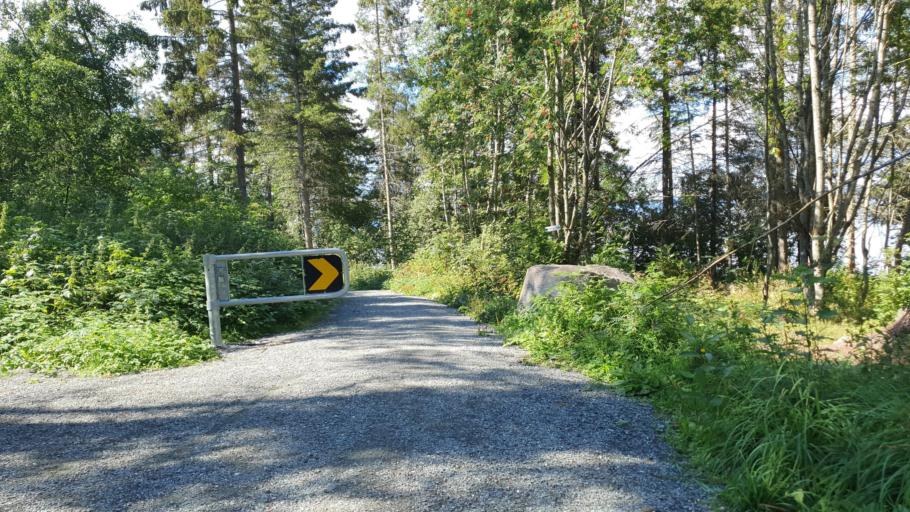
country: NO
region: Nord-Trondelag
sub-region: Levanger
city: Levanger
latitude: 63.7801
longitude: 11.3869
